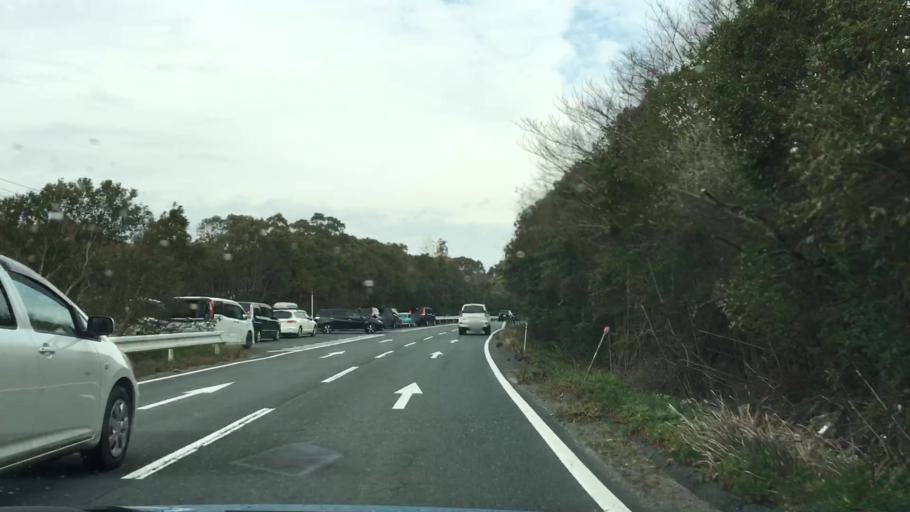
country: JP
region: Aichi
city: Tahara
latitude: 34.7000
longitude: 137.3258
